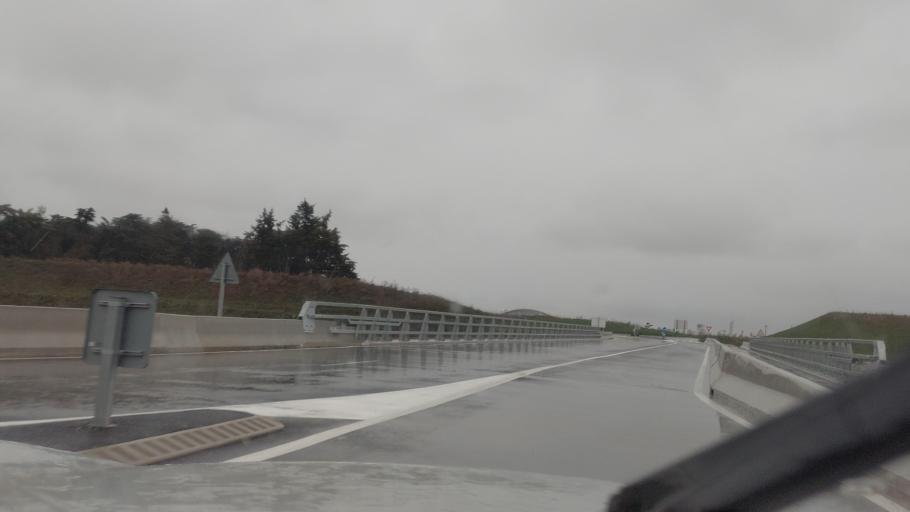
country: FR
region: Ile-de-France
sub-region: Departement de Seine-et-Marne
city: Mitry-Mory
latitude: 49.0122
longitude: 2.6027
